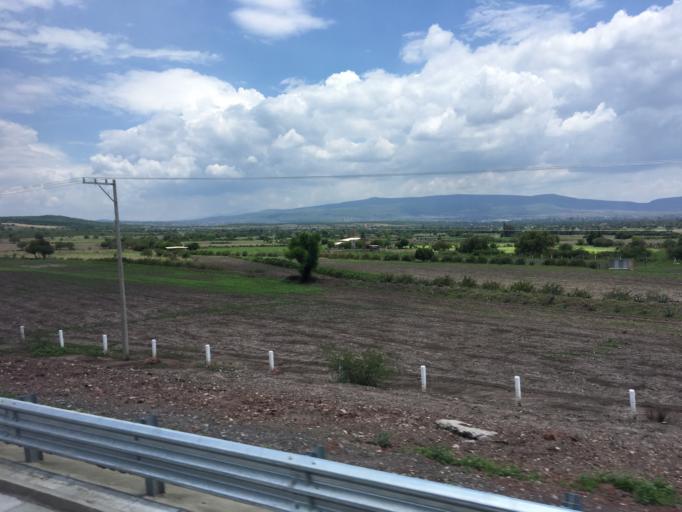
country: MX
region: Guanajuato
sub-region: Apaseo el Grande
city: Coachiti
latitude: 20.5218
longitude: -100.6115
